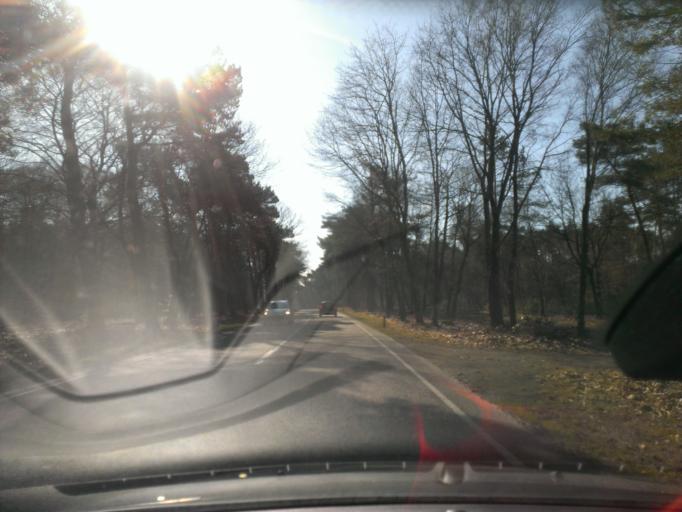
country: NL
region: Gelderland
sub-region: Gemeente Heerde
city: Heerde
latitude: 52.4199
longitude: 6.0129
